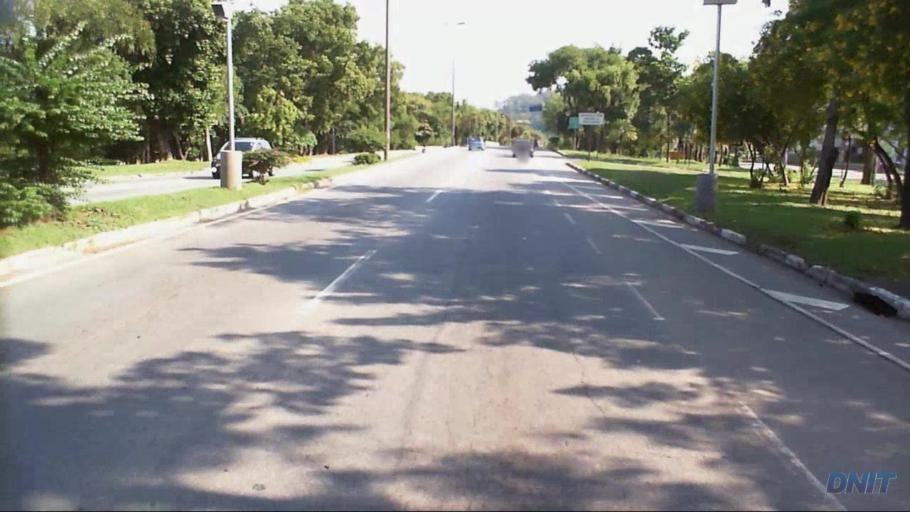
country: BR
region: Minas Gerais
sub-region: Ipatinga
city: Ipatinga
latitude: -19.5049
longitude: -42.5690
